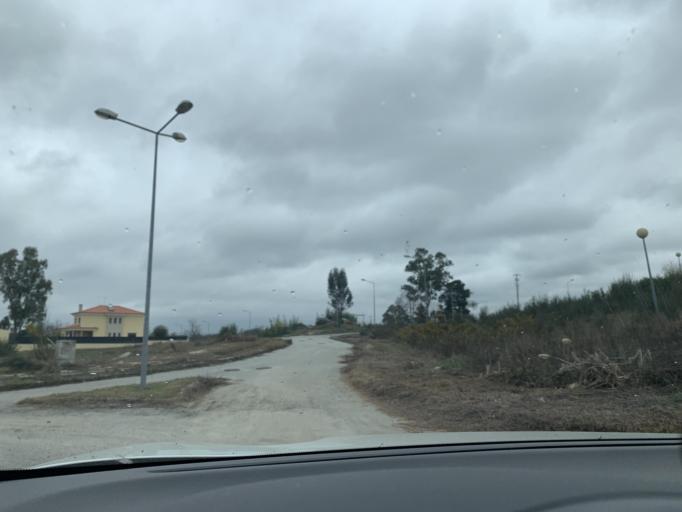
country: PT
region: Viseu
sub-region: Mangualde
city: Mangualde
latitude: 40.6096
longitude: -7.7690
